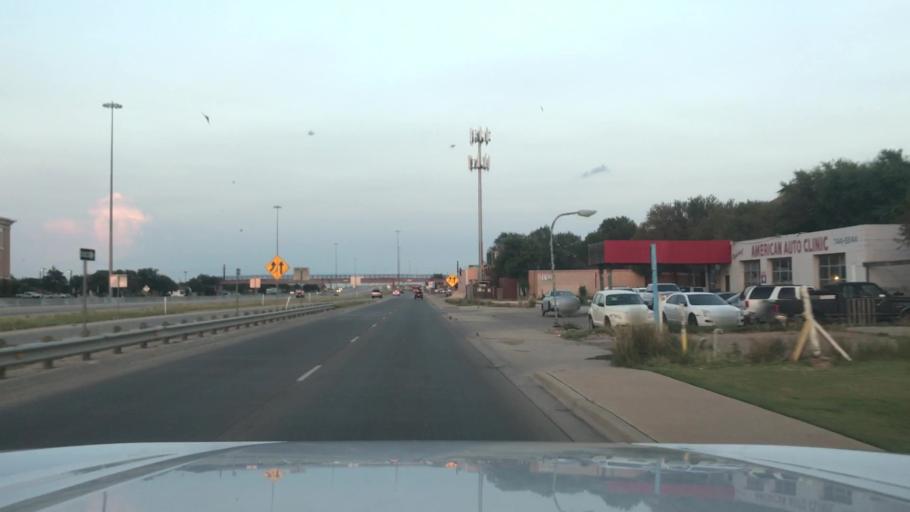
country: US
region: Texas
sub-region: Lubbock County
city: Lubbock
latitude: 33.5922
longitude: -101.8669
